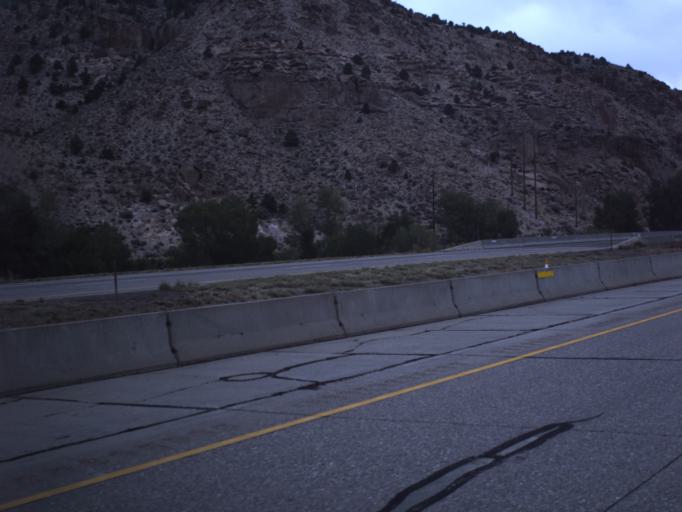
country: US
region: Utah
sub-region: Sevier County
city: Monroe
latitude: 38.5780
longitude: -112.3162
